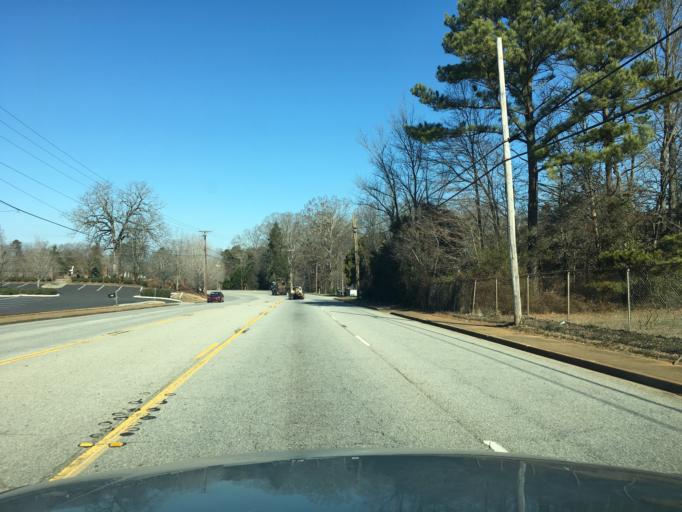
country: US
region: South Carolina
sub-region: Greenville County
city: Berea
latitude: 34.8930
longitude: -82.4699
